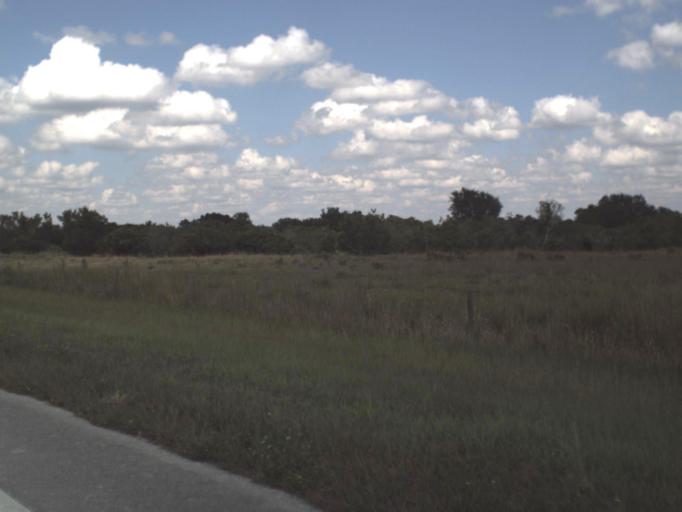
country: US
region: Florida
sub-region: Highlands County
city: Lake Placid
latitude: 27.4130
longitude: -81.1899
